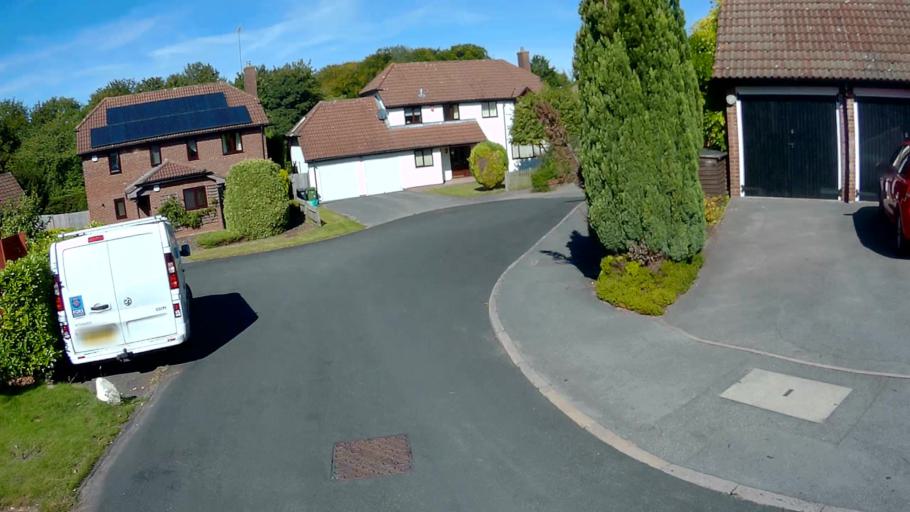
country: GB
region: England
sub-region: Hampshire
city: Basingstoke
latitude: 51.2410
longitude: -1.1307
